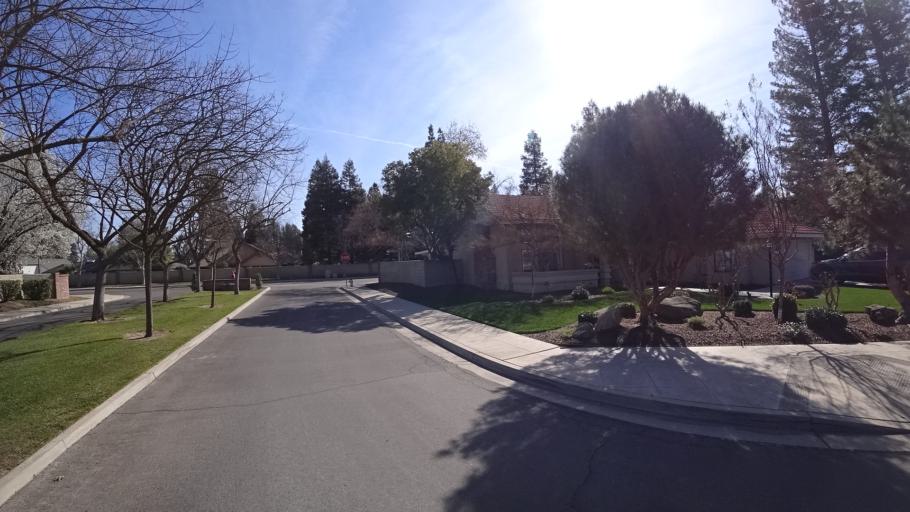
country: US
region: California
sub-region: Fresno County
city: Clovis
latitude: 36.8880
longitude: -119.7687
